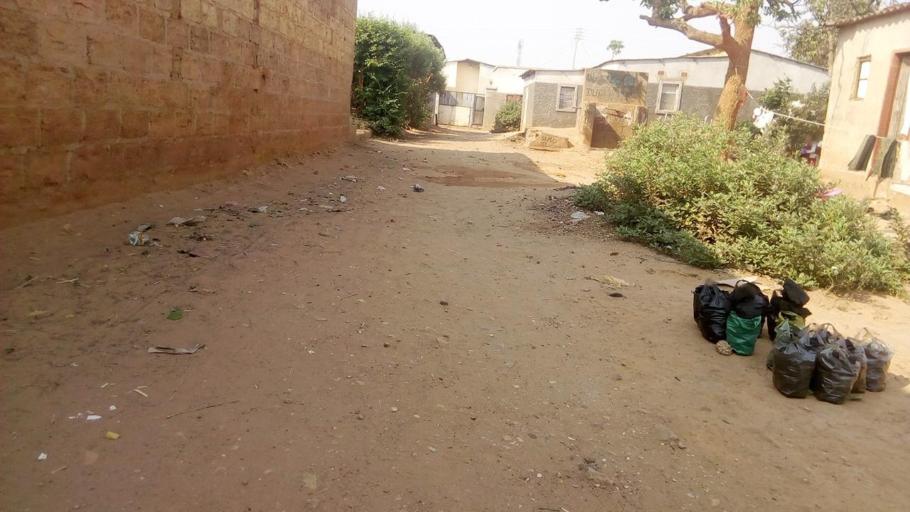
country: ZM
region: Lusaka
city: Lusaka
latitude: -15.3601
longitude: 28.2899
